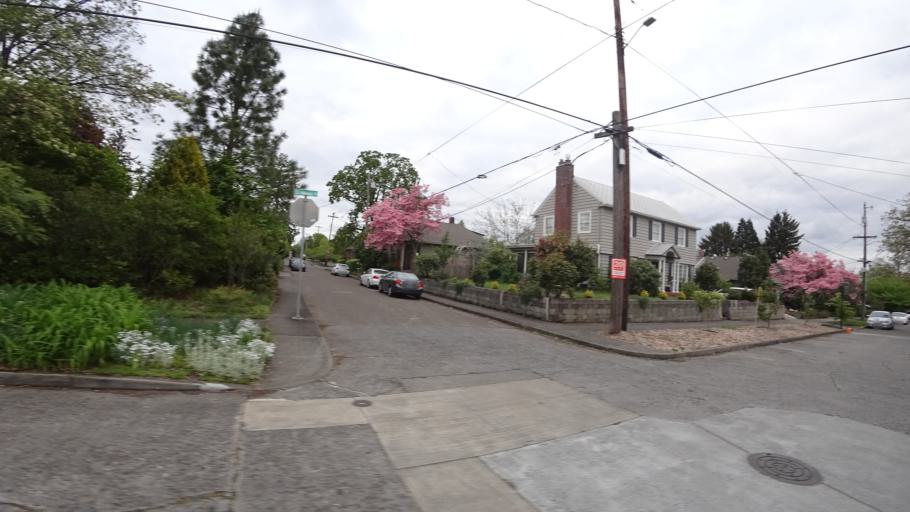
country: US
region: Oregon
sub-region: Clackamas County
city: Milwaukie
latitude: 45.4730
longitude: -122.6518
